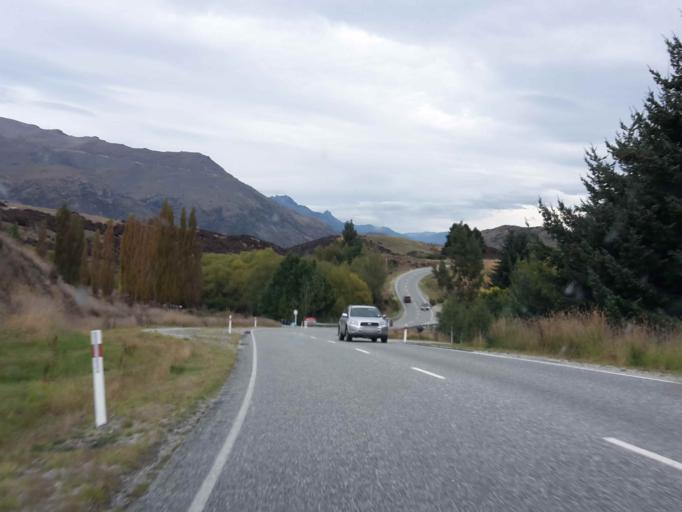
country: NZ
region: Otago
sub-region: Queenstown-Lakes District
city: Arrowtown
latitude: -44.9766
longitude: 168.8771
